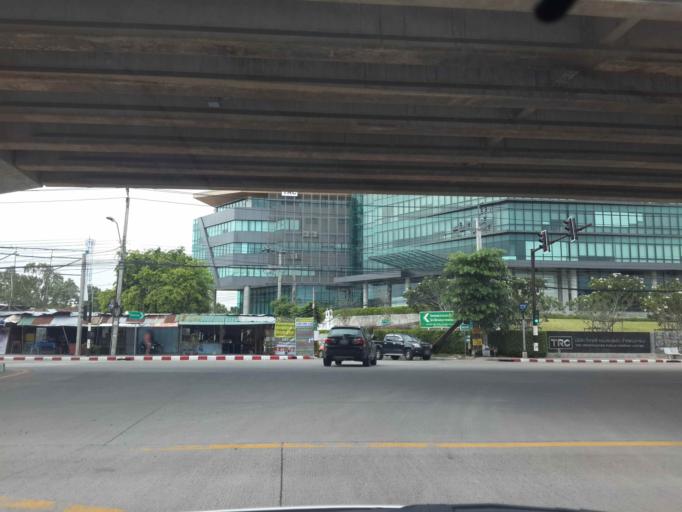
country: TH
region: Bangkok
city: Bang Khen
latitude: 13.8846
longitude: 100.6536
